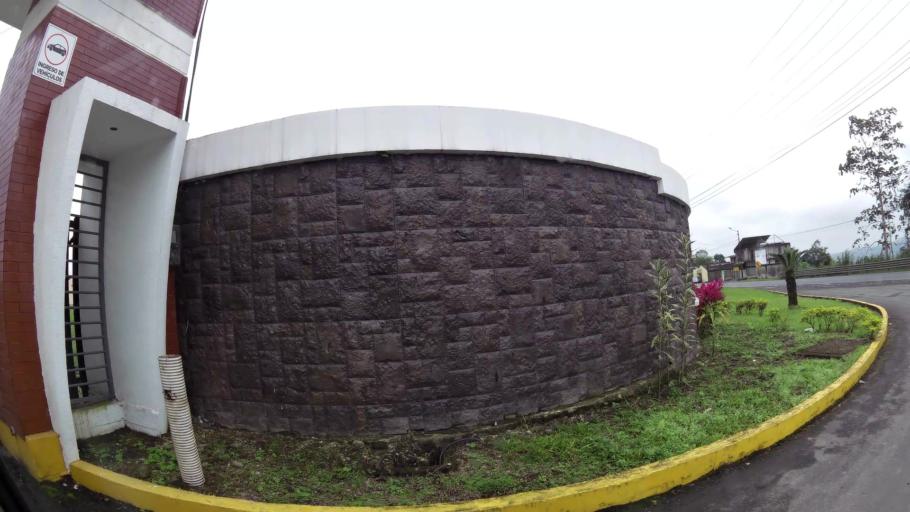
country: EC
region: Santo Domingo de los Tsachilas
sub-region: Canton Santo Domingo de los Colorados
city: Santo Domingo de los Colorados
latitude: -0.2522
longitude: -79.1371
